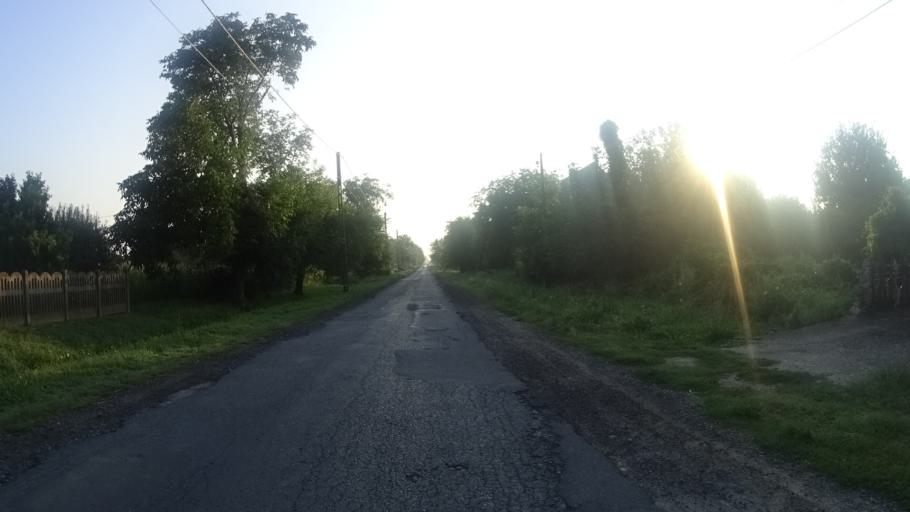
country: HU
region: Zala
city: Zalakomar
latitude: 46.5242
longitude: 17.1292
